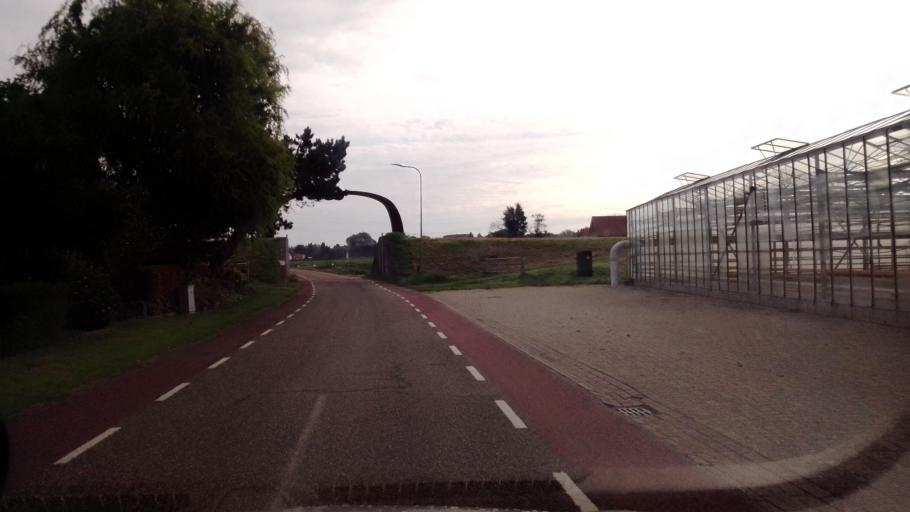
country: NL
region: Limburg
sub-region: Gemeente Venlo
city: Tegelen
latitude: 51.3314
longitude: 6.1081
